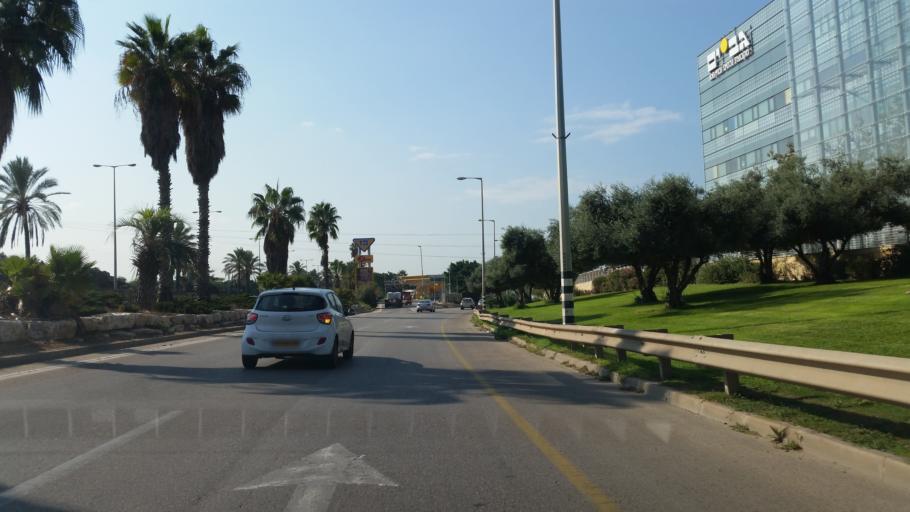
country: IL
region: Tel Aviv
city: Herzliya Pituah
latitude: 32.1577
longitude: 34.8091
